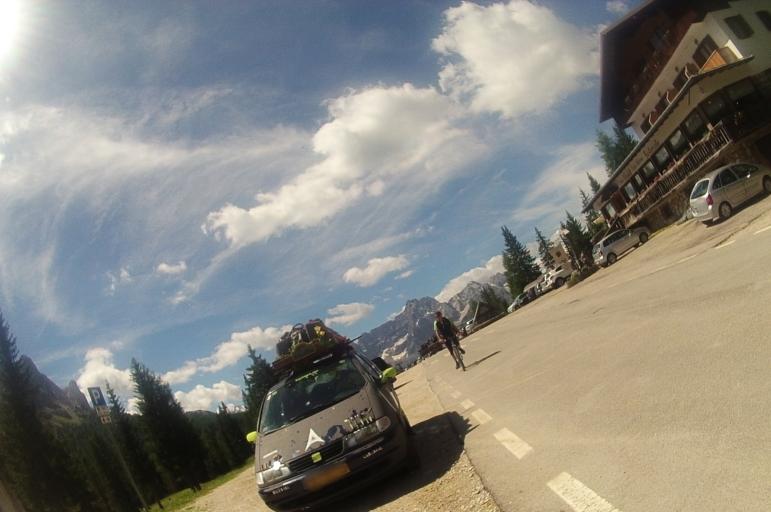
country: IT
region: Trentino-Alto Adige
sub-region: Bolzano
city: Sesto
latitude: 46.5947
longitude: 12.2642
